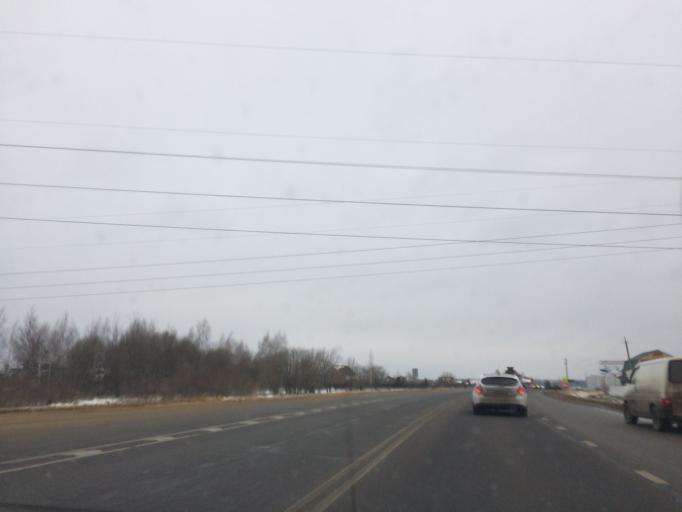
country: RU
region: Tula
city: Kosaya Gora
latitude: 54.1568
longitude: 37.4873
